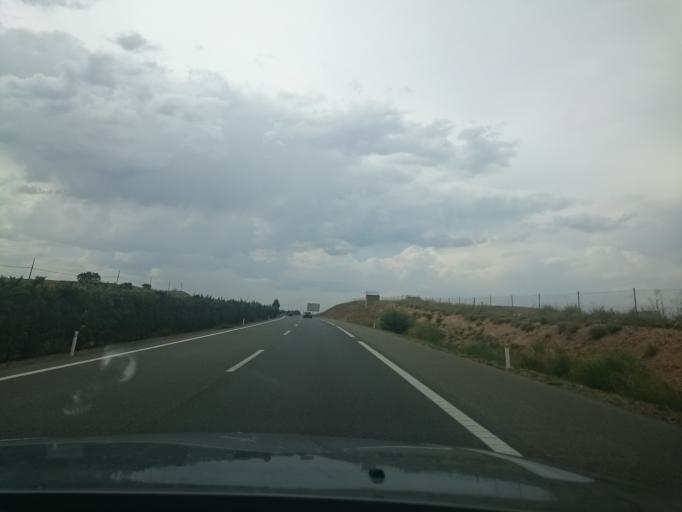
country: ES
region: Navarre
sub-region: Provincia de Navarra
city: Fontellas
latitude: 42.0092
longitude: -1.5909
